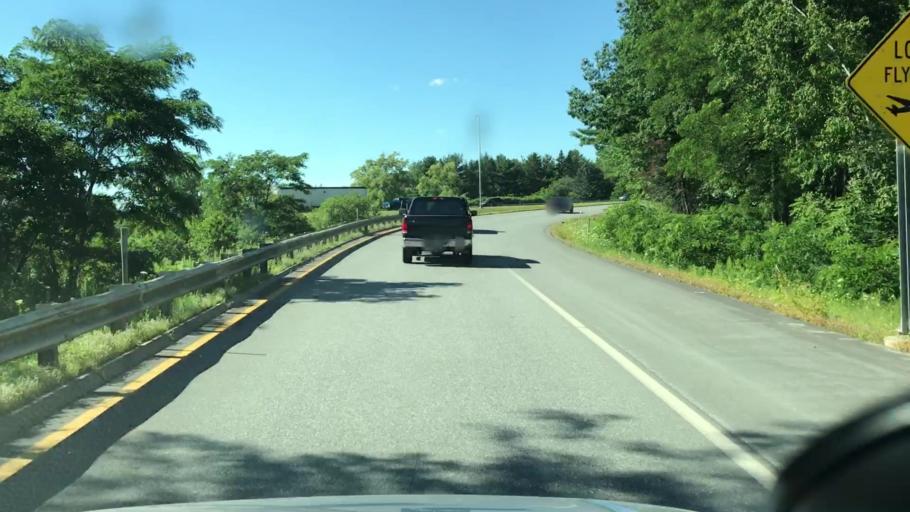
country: US
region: Maine
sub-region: Penobscot County
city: Bangor
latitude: 44.7886
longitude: -68.8057
